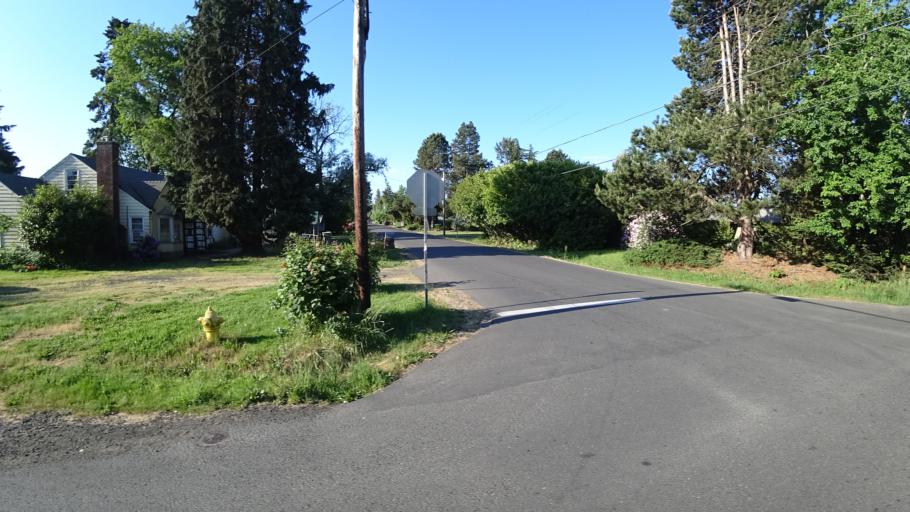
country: US
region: Oregon
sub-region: Washington County
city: Aloha
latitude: 45.5004
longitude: -122.8751
